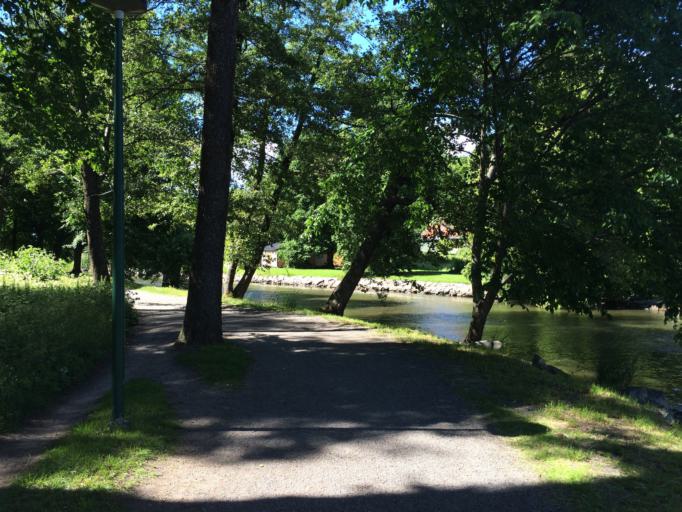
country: SE
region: Stockholm
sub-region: Nacka Kommun
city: Nacka
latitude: 59.3262
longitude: 18.1488
